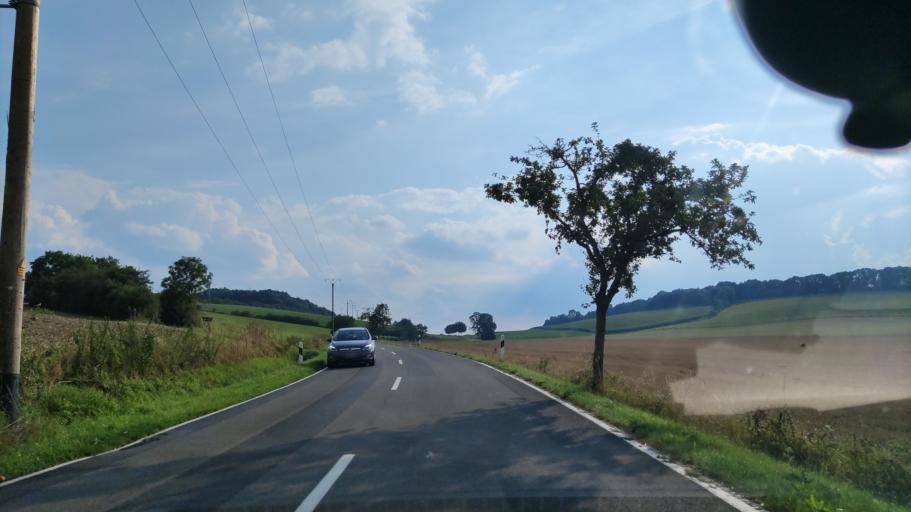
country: DE
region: Lower Saxony
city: Dassel
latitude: 51.8166
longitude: 9.7077
